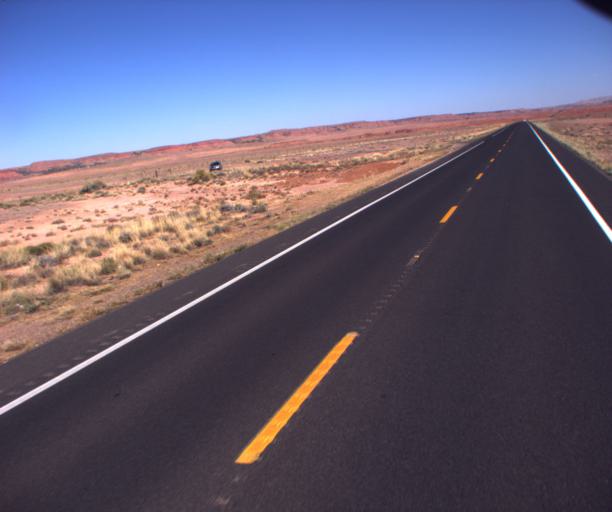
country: US
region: Arizona
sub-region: Coconino County
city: Tuba City
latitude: 36.0963
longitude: -111.3564
